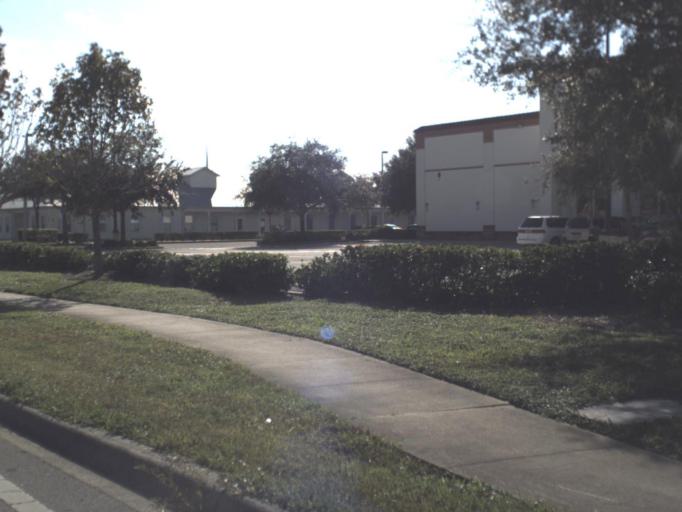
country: US
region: Florida
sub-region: Brevard County
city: South Patrick Shores
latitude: 28.1574
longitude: -80.6721
